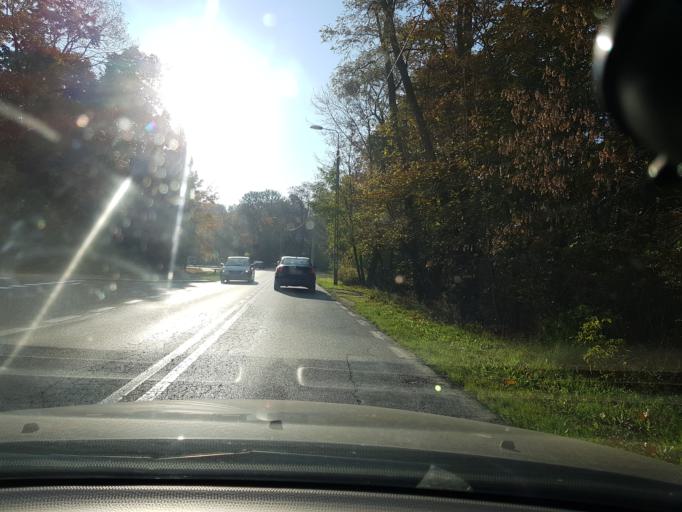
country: PL
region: Masovian Voivodeship
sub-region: Warszawa
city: Bemowo
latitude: 52.2647
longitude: 20.8845
